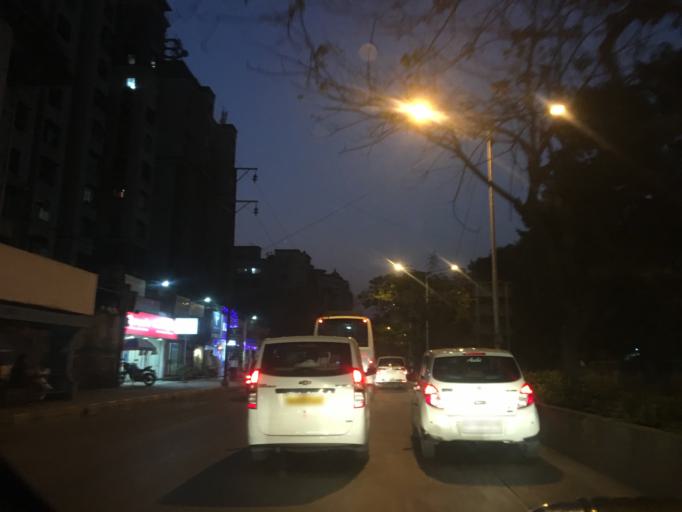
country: IN
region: Maharashtra
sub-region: Thane
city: Airoli
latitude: 19.1480
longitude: 72.9990
